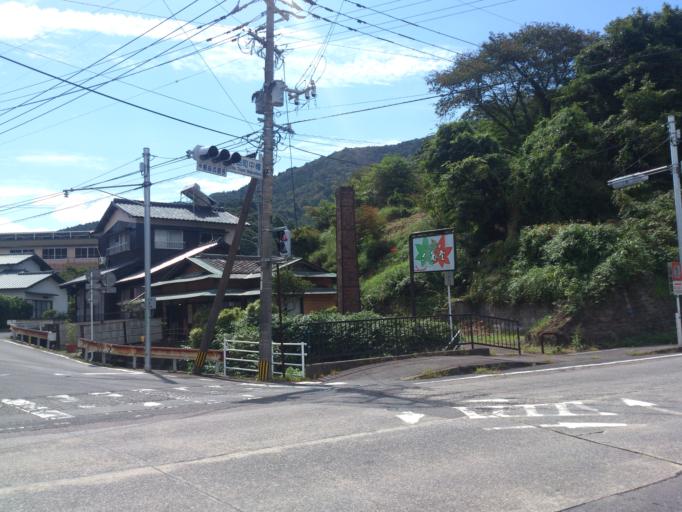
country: JP
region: Saga Prefecture
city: Imaricho-ko
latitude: 33.1896
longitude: 129.9058
